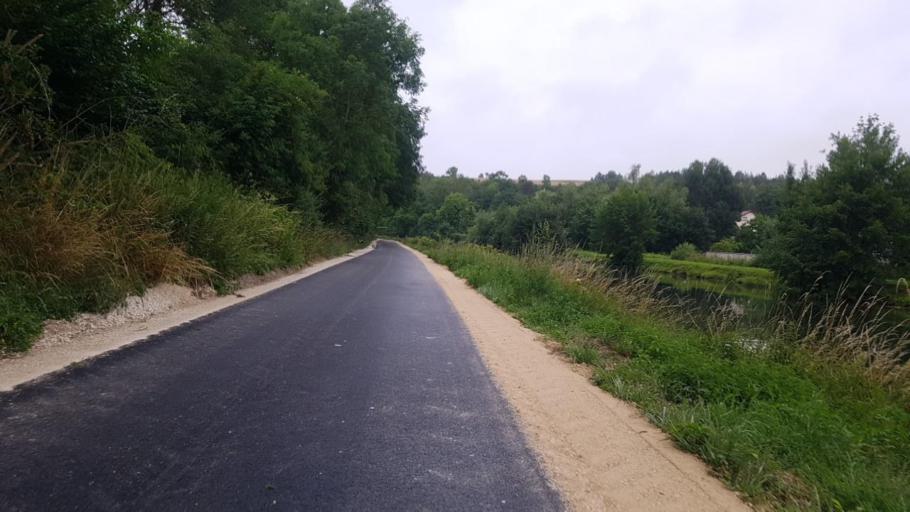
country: FR
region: Champagne-Ardenne
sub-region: Departement de la Marne
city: Vitry-le-Francois
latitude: 48.7915
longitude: 4.5330
